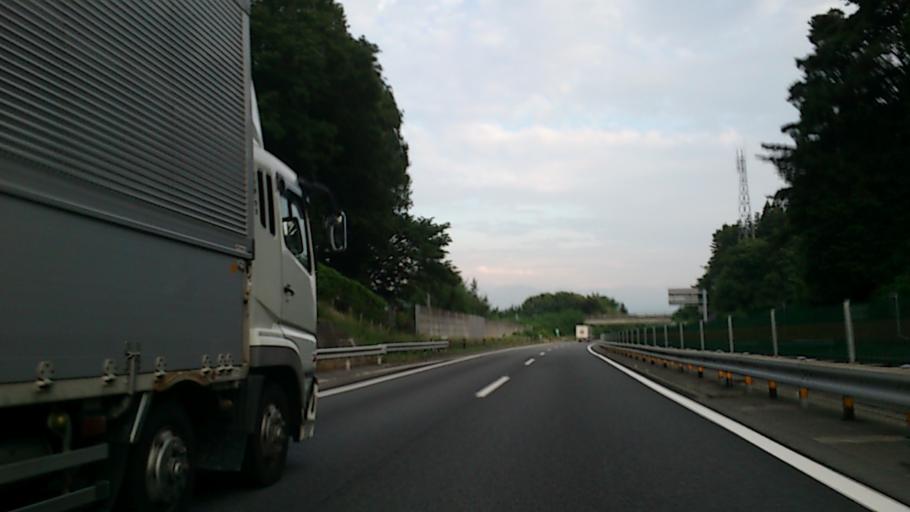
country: JP
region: Nagano
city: Ina
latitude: 35.7024
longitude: 137.9095
